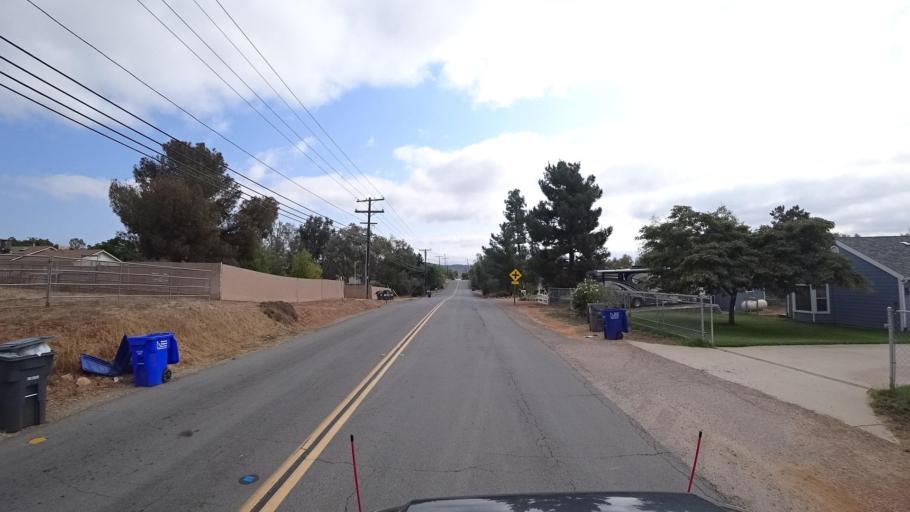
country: US
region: California
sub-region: San Diego County
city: Ramona
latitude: 33.0348
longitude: -116.8493
